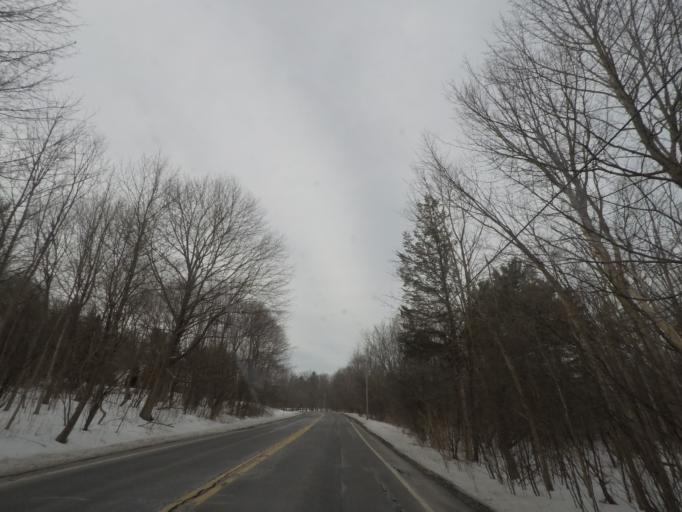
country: US
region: New York
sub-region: Albany County
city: Altamont
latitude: 42.6632
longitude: -74.0003
